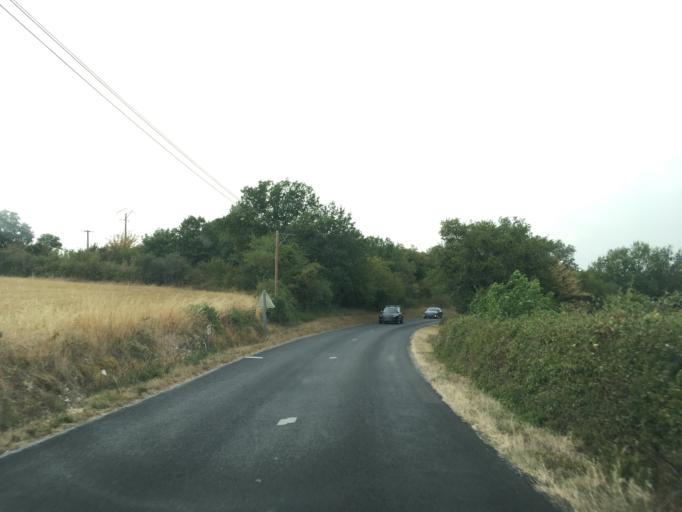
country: FR
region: Midi-Pyrenees
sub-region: Departement du Lot
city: Souillac
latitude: 44.8238
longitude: 1.5735
